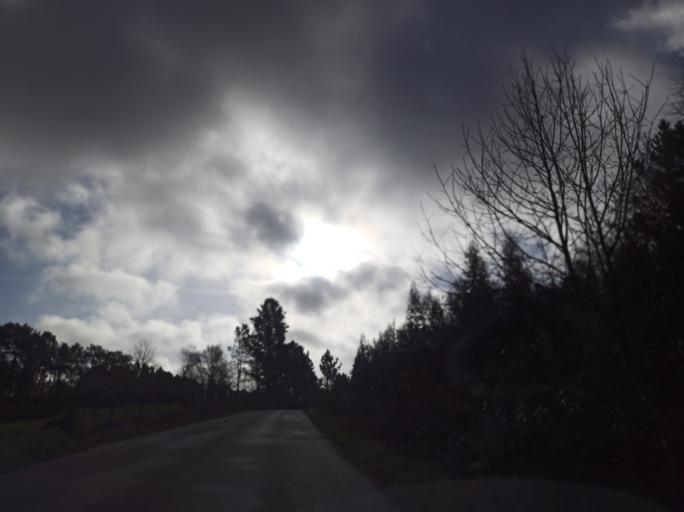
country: ES
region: Galicia
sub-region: Provincia da Coruna
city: Curtis
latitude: 43.0965
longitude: -7.9765
